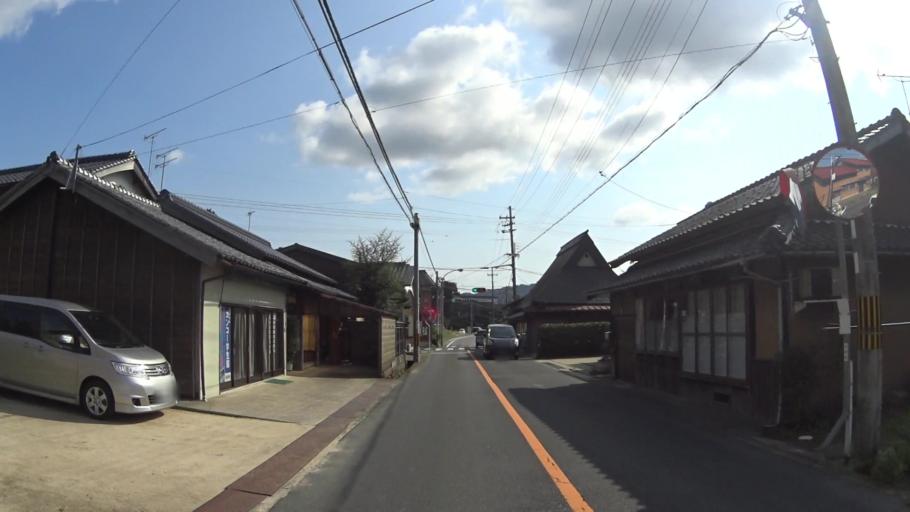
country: JP
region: Kyoto
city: Miyazu
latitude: 35.5868
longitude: 135.1020
